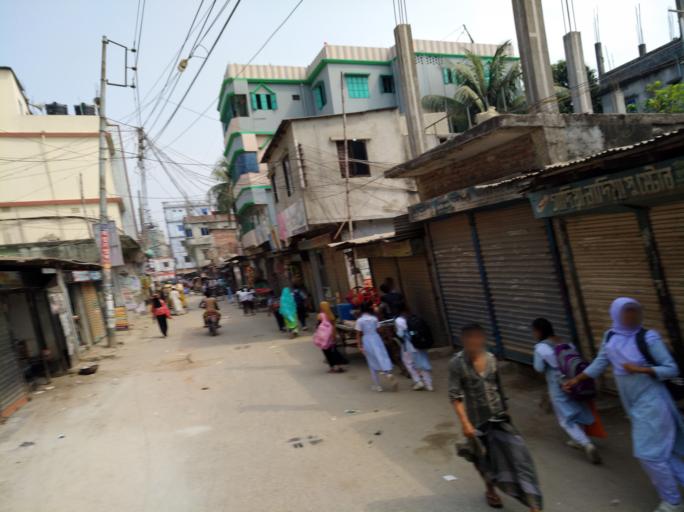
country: BD
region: Dhaka
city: Azimpur
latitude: 23.7159
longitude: 90.3750
